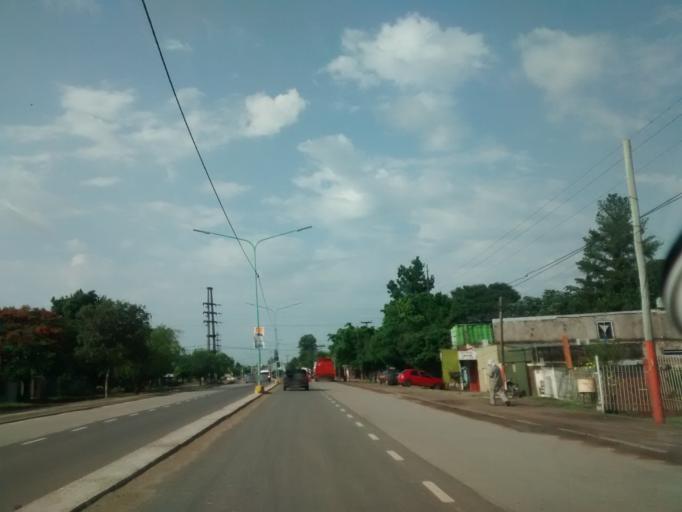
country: AR
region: Chaco
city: Resistencia
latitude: -27.4227
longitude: -58.9760
